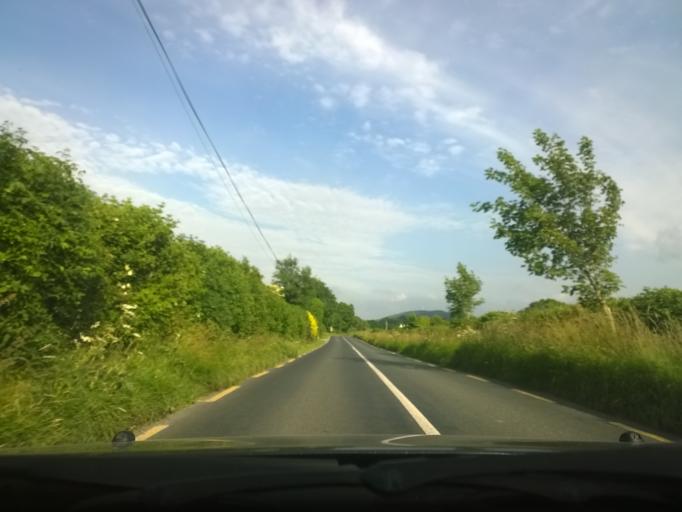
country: IE
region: Leinster
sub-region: Kildare
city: Rathangan
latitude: 53.2160
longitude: -6.9754
